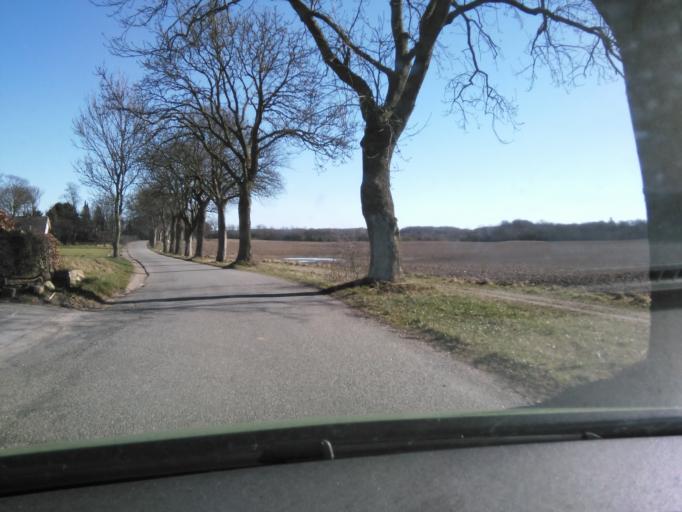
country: DK
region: Central Jutland
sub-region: Arhus Kommune
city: Marslet
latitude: 56.0726
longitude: 10.1792
